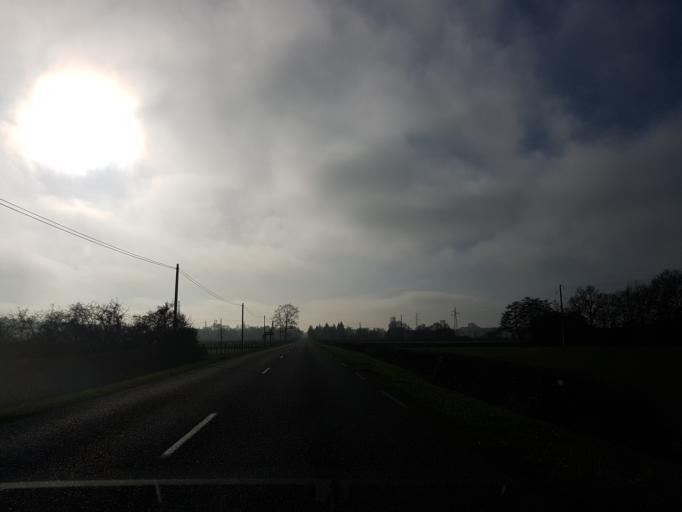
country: FR
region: Bourgogne
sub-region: Departement de Saone-et-Loire
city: Gueugnon
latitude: 46.6167
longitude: 4.0795
